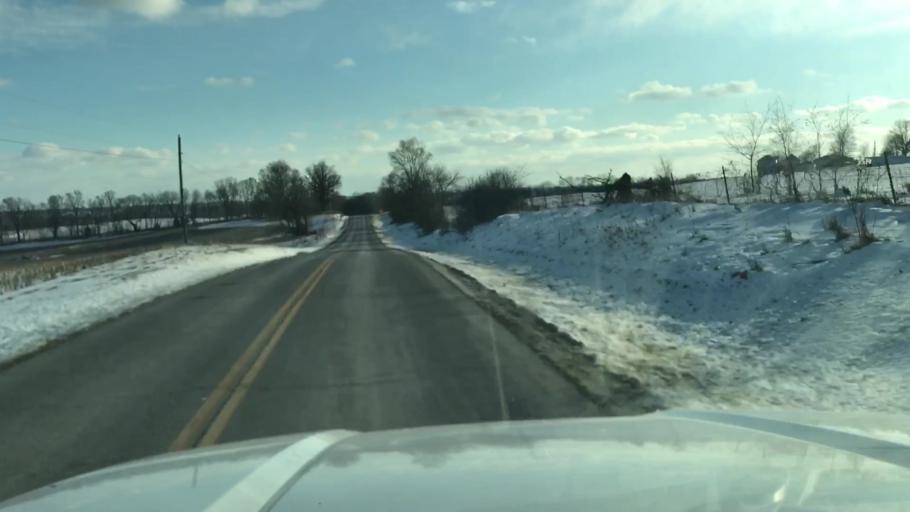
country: US
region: Missouri
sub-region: Andrew County
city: Savannah
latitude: 40.0497
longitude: -94.9750
